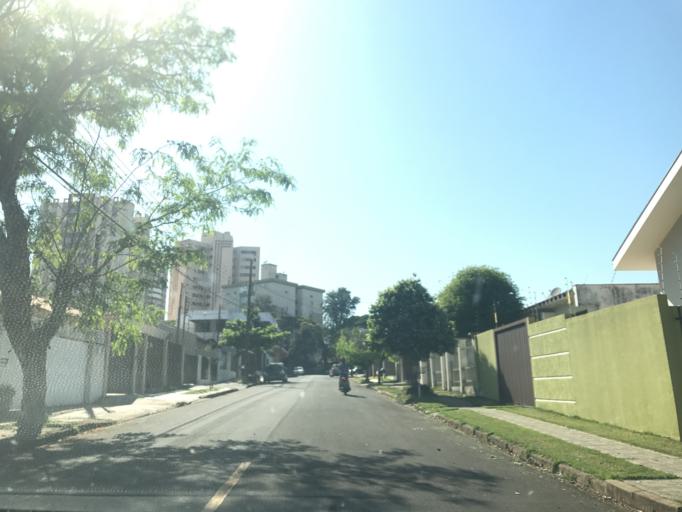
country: BR
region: Parana
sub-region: Maringa
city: Maringa
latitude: -23.4418
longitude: -51.9342
